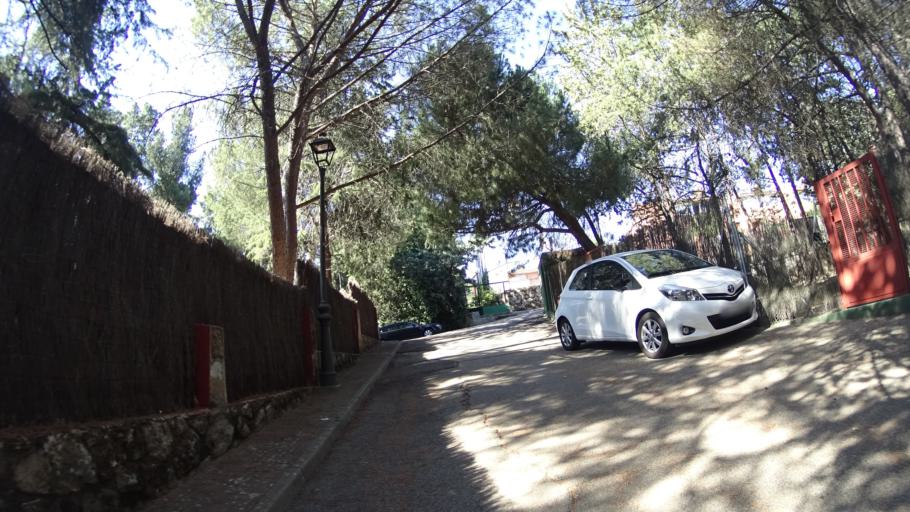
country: ES
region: Madrid
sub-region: Provincia de Madrid
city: Galapagar
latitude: 40.5934
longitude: -3.9817
